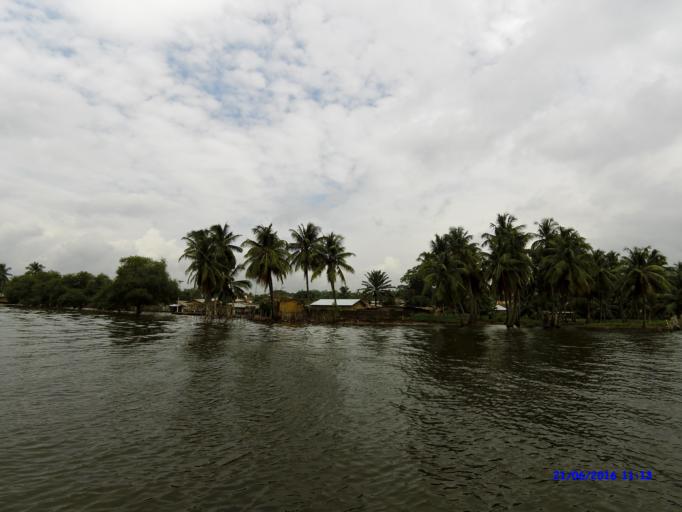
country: BJ
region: Mono
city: Come
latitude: 6.5274
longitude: 1.9707
